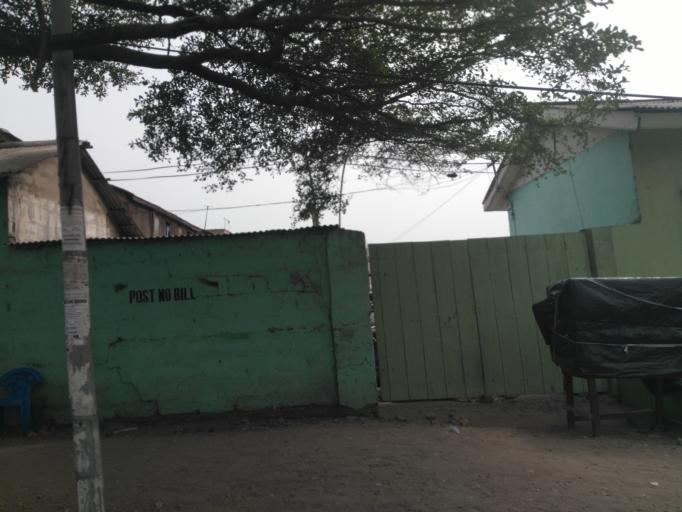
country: GH
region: Greater Accra
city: Accra
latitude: 5.5384
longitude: -0.2162
